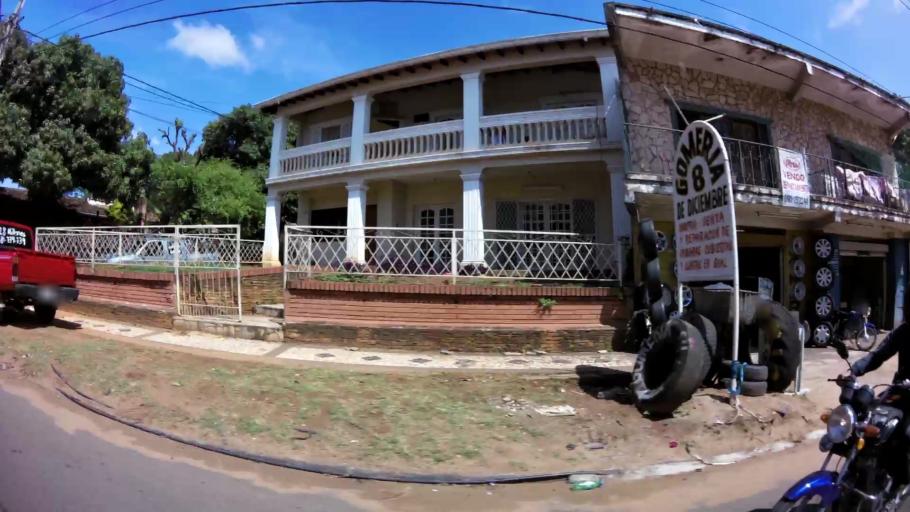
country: PY
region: Central
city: San Lorenzo
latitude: -25.3178
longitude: -57.5077
